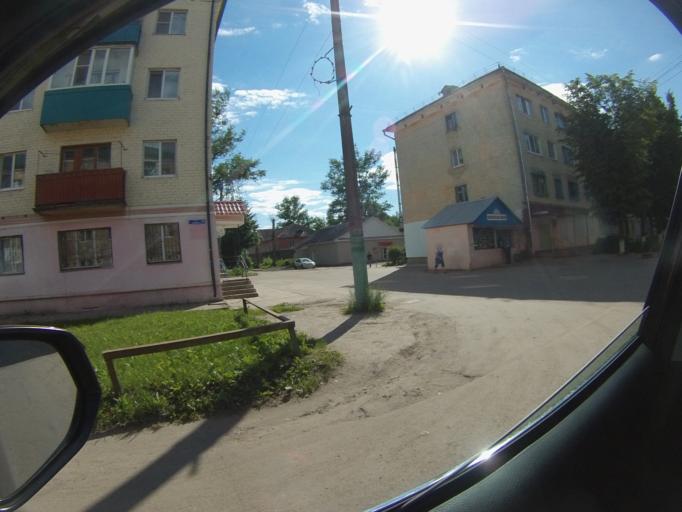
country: RU
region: Orjol
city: Mtsensk
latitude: 53.2769
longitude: 36.5761
